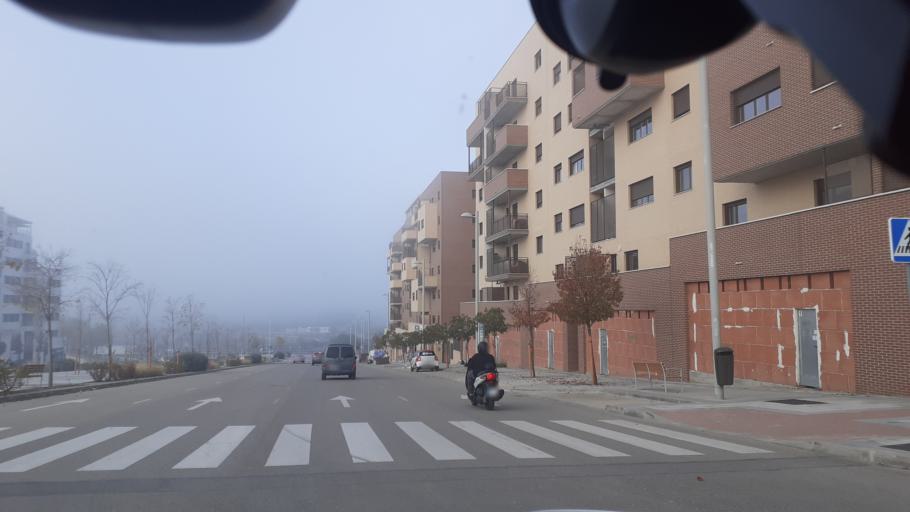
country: ES
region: Madrid
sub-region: Provincia de Madrid
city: Coslada
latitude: 40.4074
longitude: -3.5525
